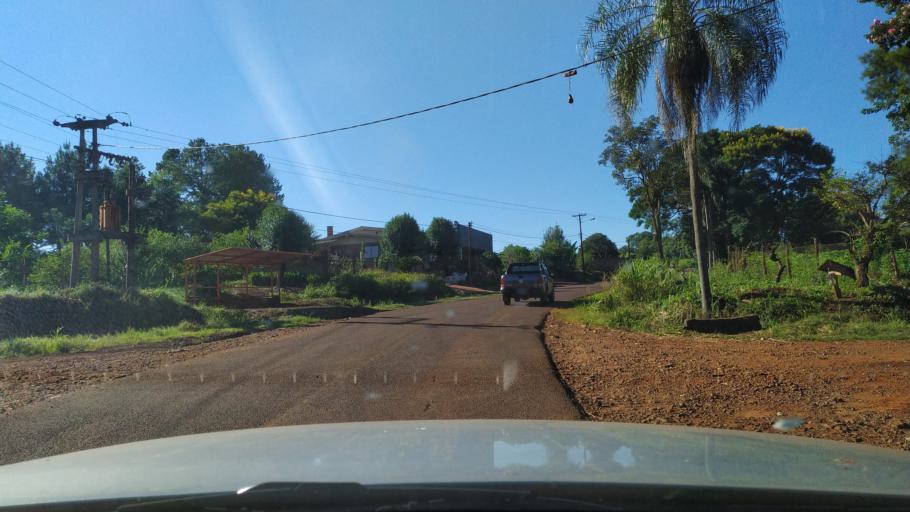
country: AR
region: Misiones
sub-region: Departamento de Montecarlo
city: Montecarlo
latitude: -26.6002
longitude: -54.7023
